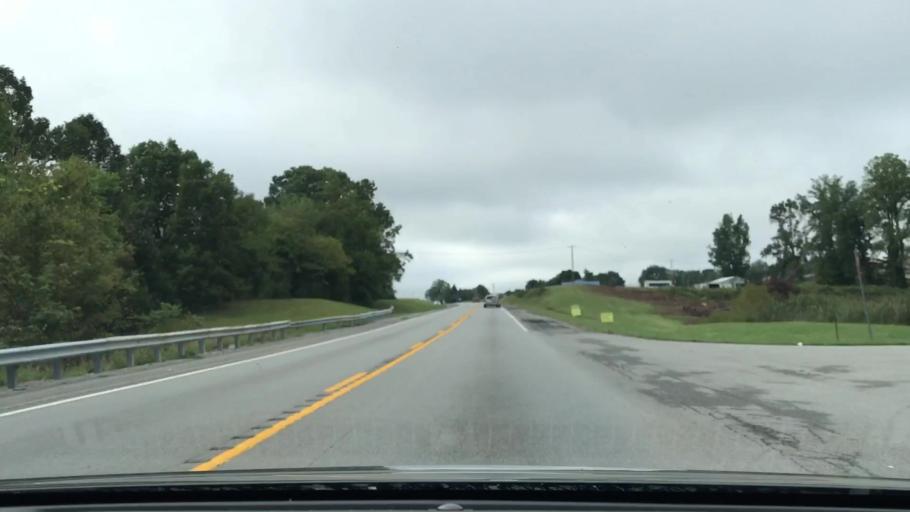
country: US
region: Kentucky
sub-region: Russell County
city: Russell Springs
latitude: 37.0424
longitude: -85.0724
